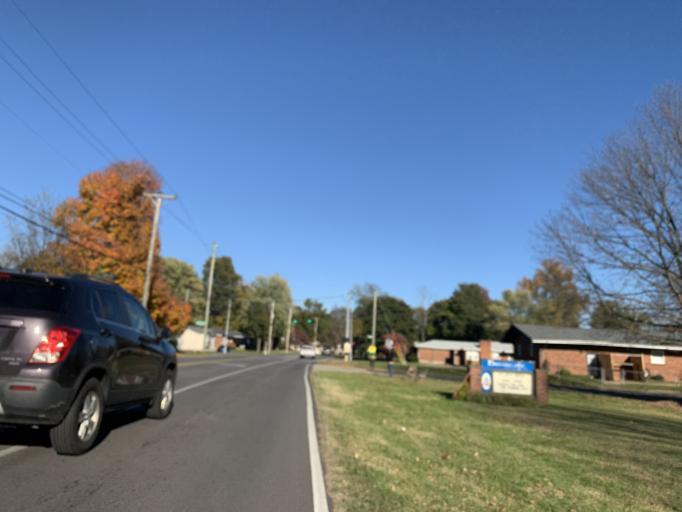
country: US
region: Kentucky
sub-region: Jefferson County
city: Saint Dennis
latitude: 38.1682
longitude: -85.8359
